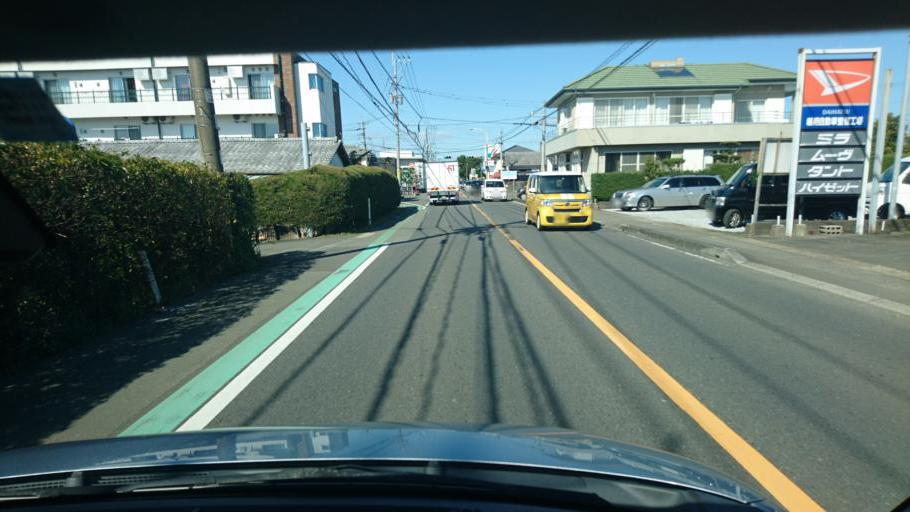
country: JP
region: Miyazaki
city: Miyazaki-shi
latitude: 31.8624
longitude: 131.4326
